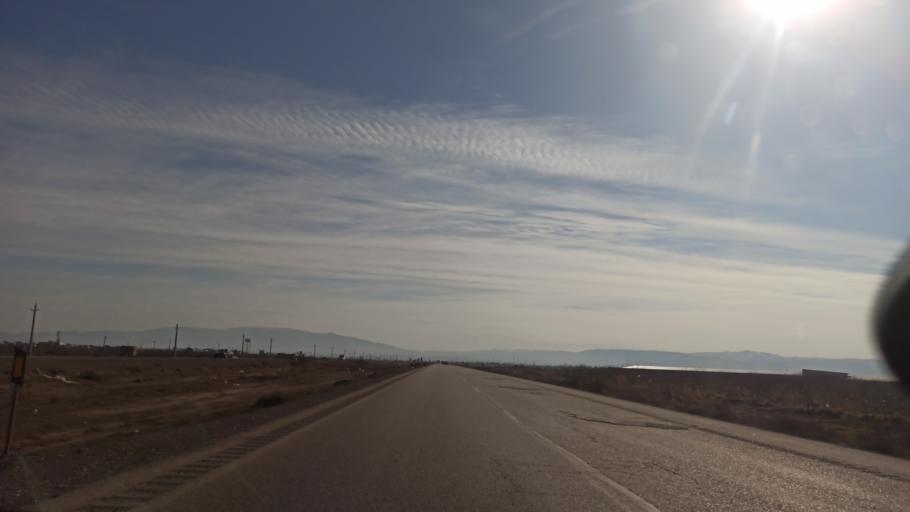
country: IR
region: Qazvin
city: Bu'in Zahra
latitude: 35.8024
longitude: 50.0759
